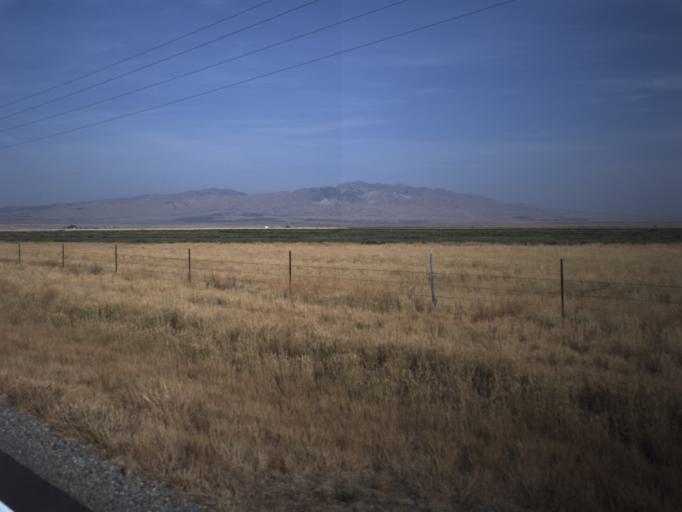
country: US
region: Idaho
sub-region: Oneida County
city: Malad City
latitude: 41.9672
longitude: -112.8545
